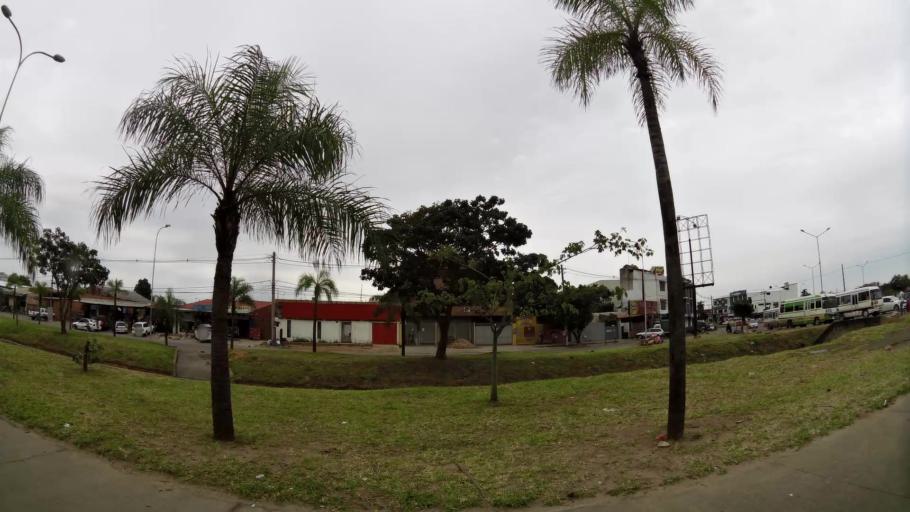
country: BO
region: Santa Cruz
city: Santa Cruz de la Sierra
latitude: -17.8229
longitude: -63.1853
